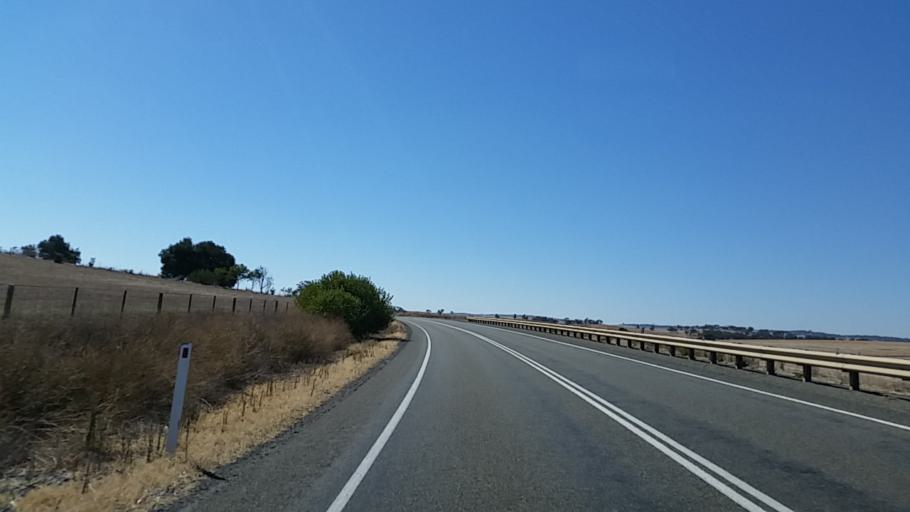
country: AU
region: South Australia
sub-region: Clare and Gilbert Valleys
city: Clare
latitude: -34.0673
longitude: 138.7907
